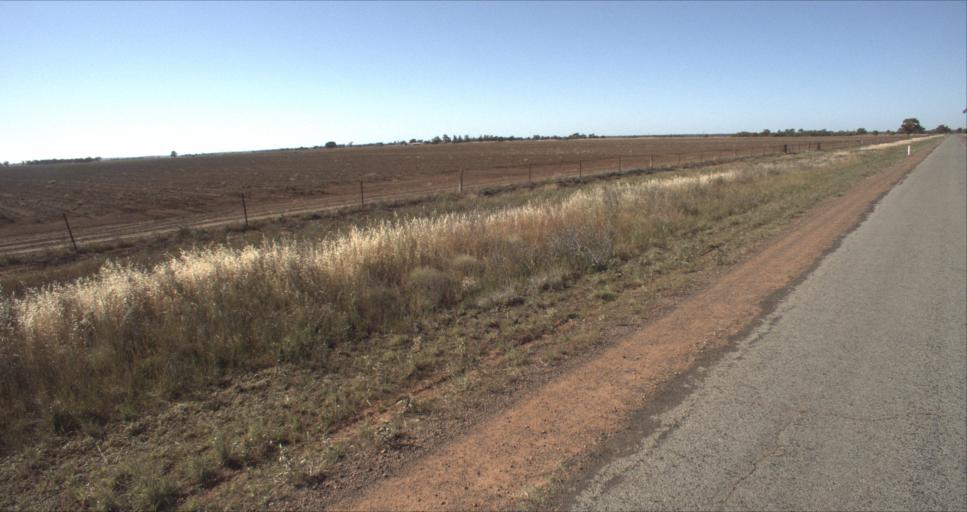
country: AU
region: New South Wales
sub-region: Leeton
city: Leeton
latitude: -34.5598
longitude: 146.3129
